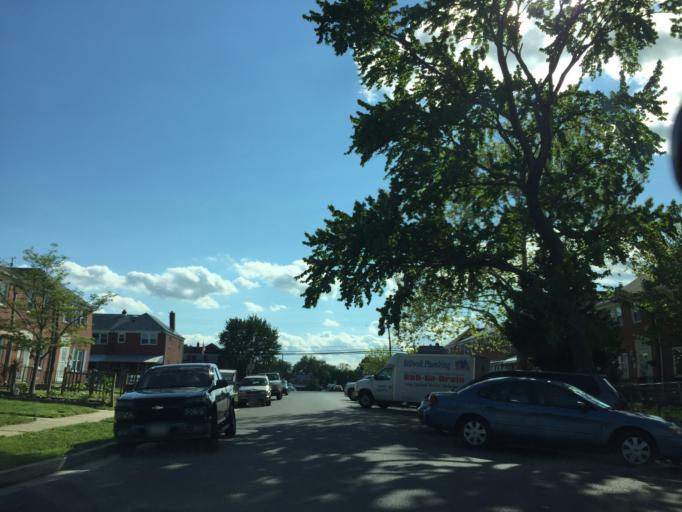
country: US
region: Maryland
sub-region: Baltimore County
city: Middle River
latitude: 39.3273
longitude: -76.4377
